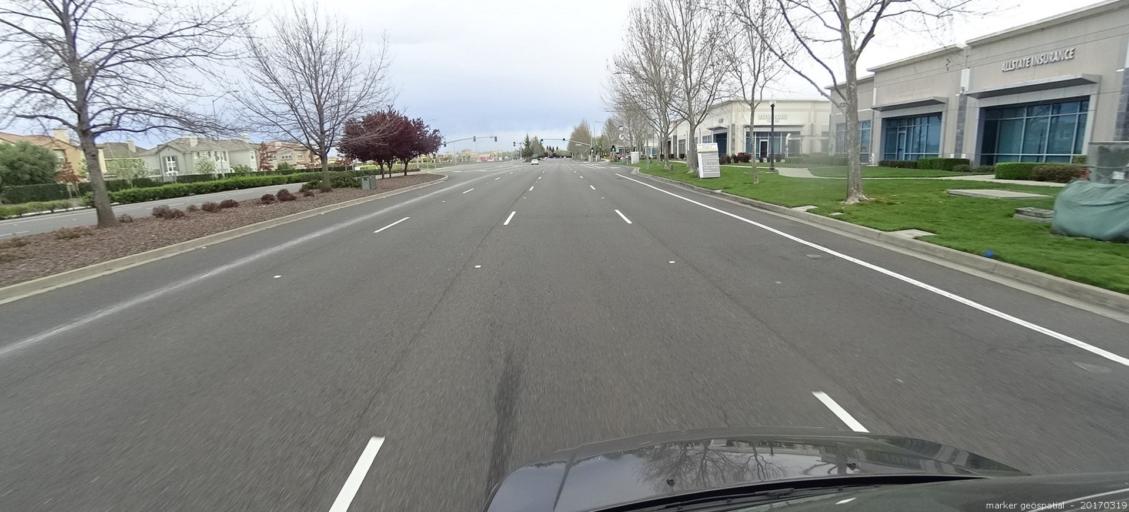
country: US
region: California
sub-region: Sacramento County
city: Sacramento
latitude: 38.6426
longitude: -121.5088
